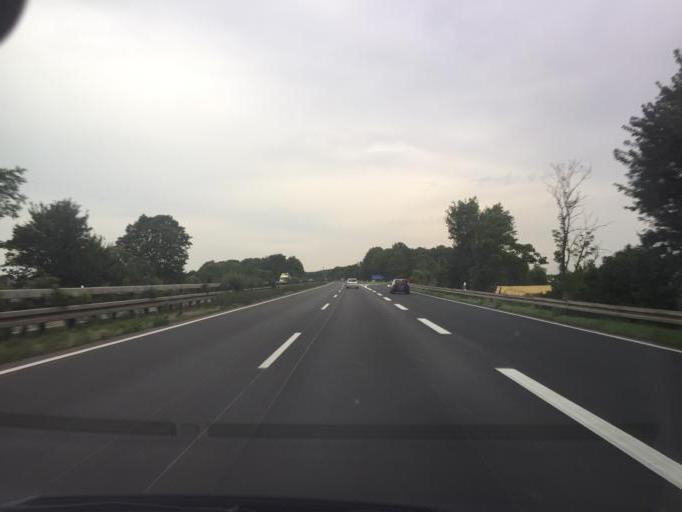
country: DE
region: North Rhine-Westphalia
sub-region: Regierungsbezirk Dusseldorf
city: Viersen
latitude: 51.2395
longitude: 6.3605
